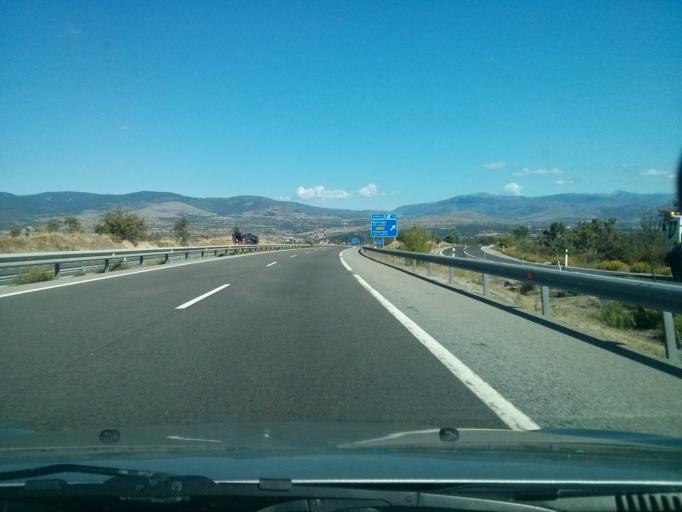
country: ES
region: Madrid
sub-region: Provincia de Madrid
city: Buitrago del Lozoya
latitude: 40.9662
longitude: -3.6412
